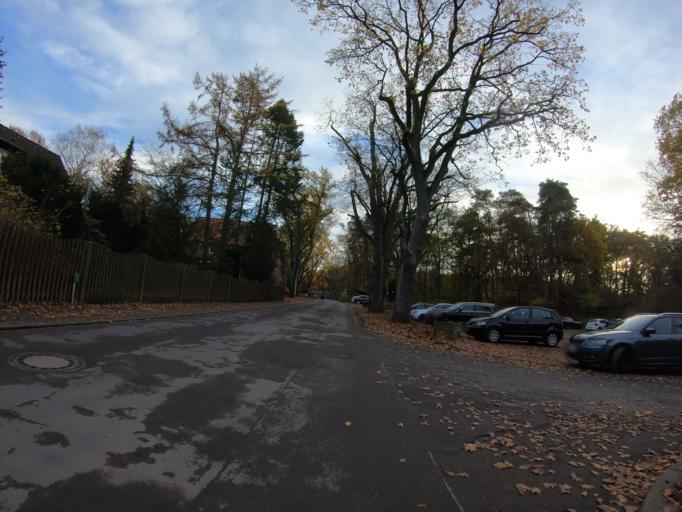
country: DE
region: Lower Saxony
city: Ribbesbuttel
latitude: 52.4584
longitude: 10.4962
